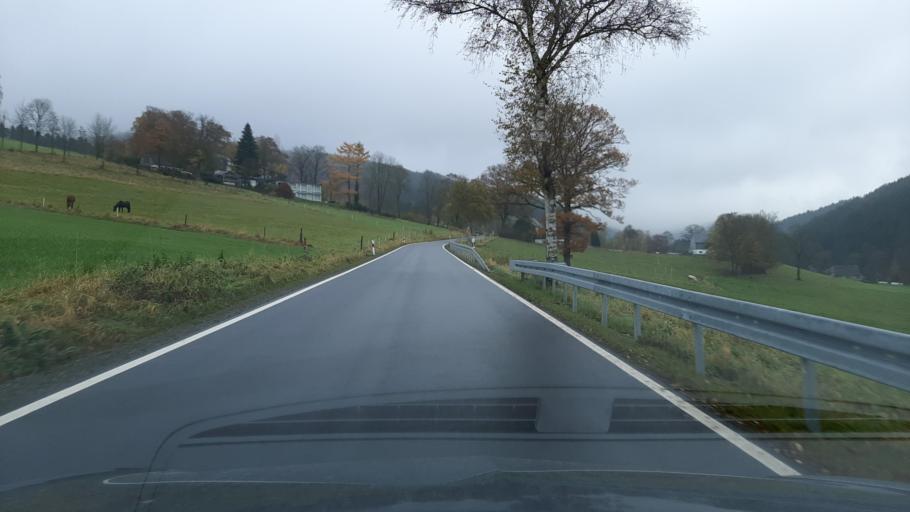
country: DE
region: North Rhine-Westphalia
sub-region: Regierungsbezirk Arnsberg
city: Bad Fredeburg
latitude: 51.1915
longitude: 8.3749
